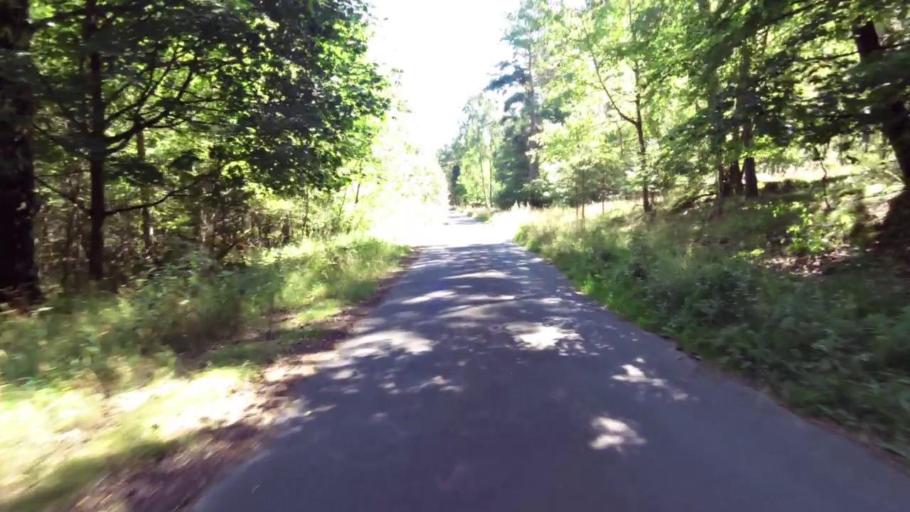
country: PL
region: West Pomeranian Voivodeship
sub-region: Powiat szczecinecki
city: Borne Sulinowo
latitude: 53.5996
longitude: 16.6150
